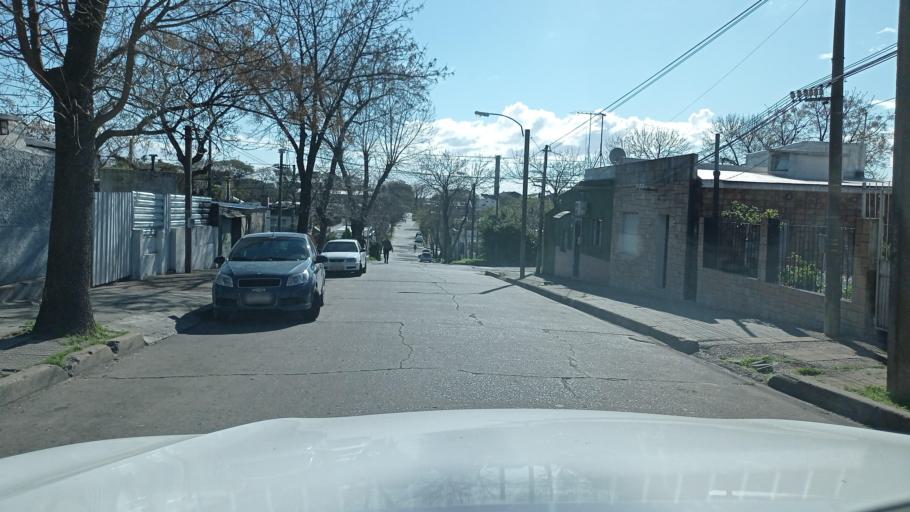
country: UY
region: Montevideo
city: Montevideo
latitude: -34.8533
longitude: -56.1678
